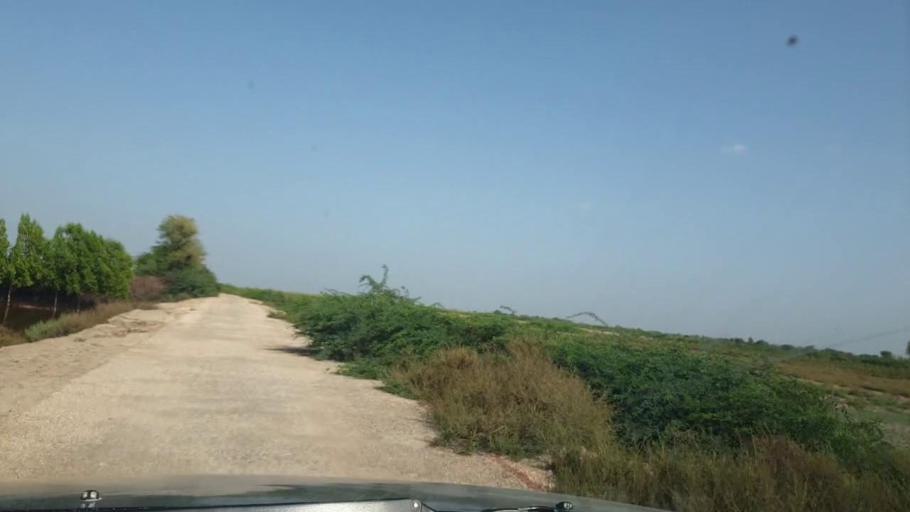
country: PK
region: Sindh
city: Mirwah Gorchani
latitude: 25.2443
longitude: 68.9537
